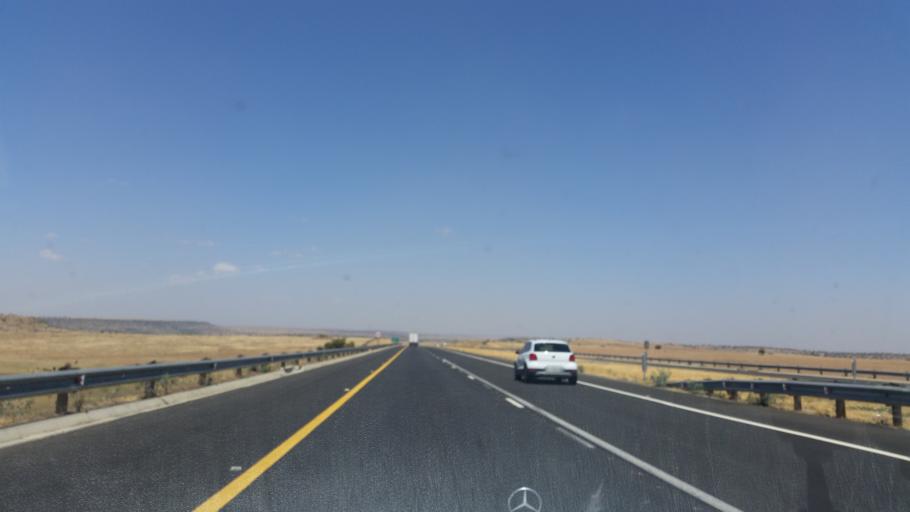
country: ZA
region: Orange Free State
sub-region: Lejweleputswa District Municipality
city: Winburg
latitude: -28.5060
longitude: 26.9946
